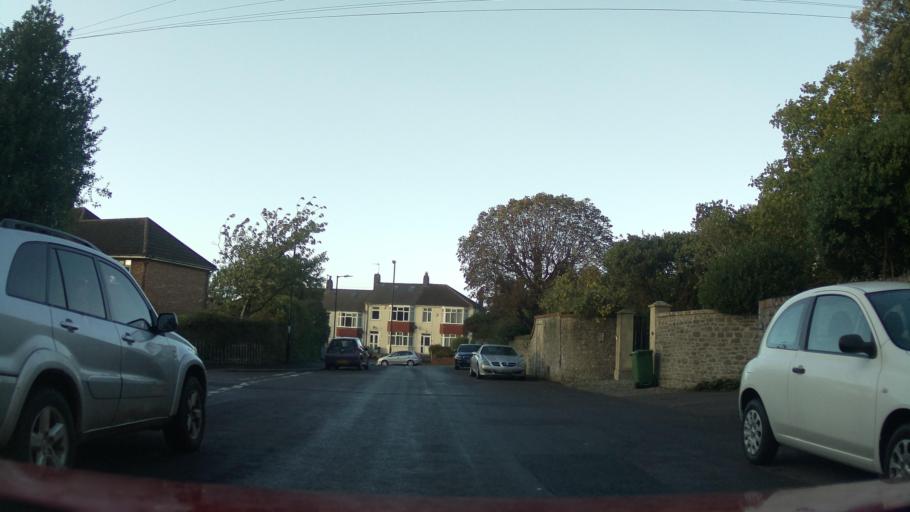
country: GB
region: England
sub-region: Bristol
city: Bristol
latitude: 51.4918
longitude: -2.6123
